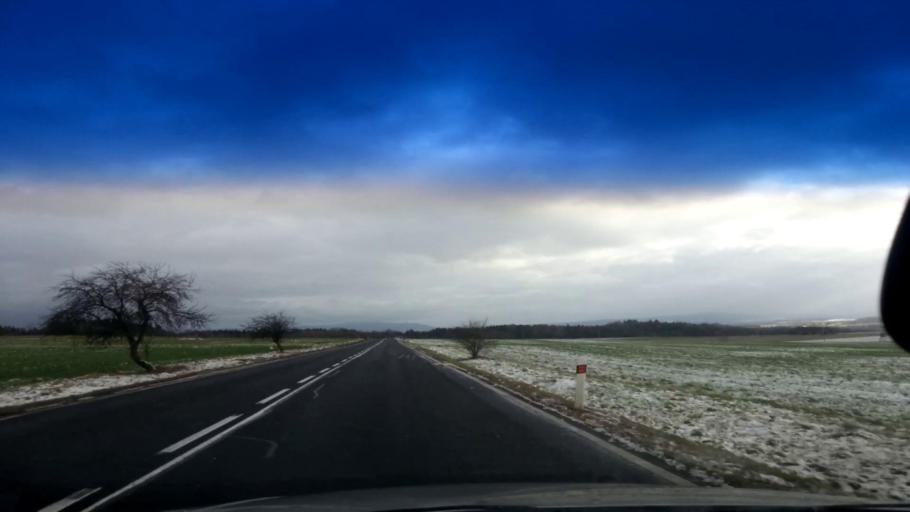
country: CZ
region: Karlovarsky
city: Hazlov
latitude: 50.1435
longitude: 12.3049
